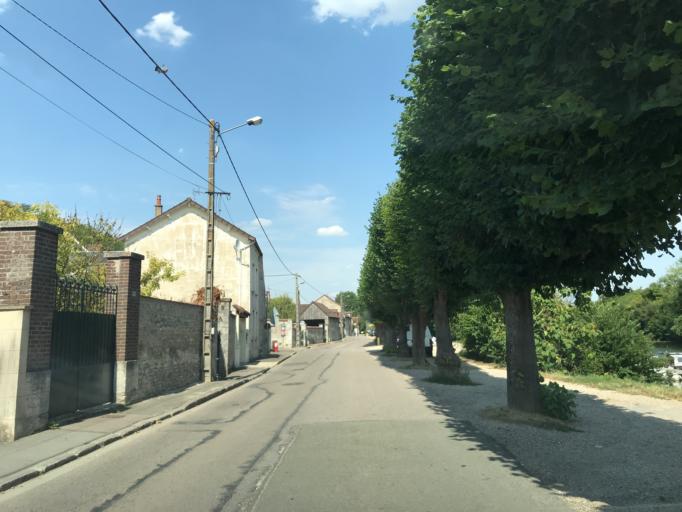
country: FR
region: Ile-de-France
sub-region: Departement des Yvelines
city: Bonnieres-sur-Seine
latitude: 49.0425
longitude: 1.5749
